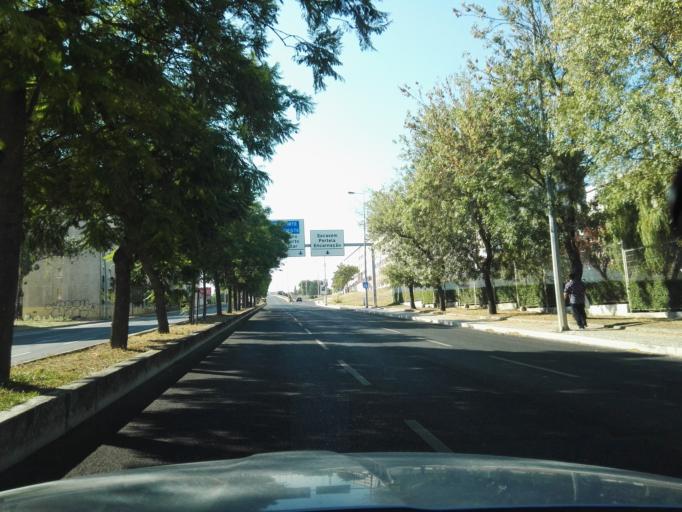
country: PT
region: Lisbon
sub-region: Loures
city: Moscavide
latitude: 38.7792
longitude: -9.1162
